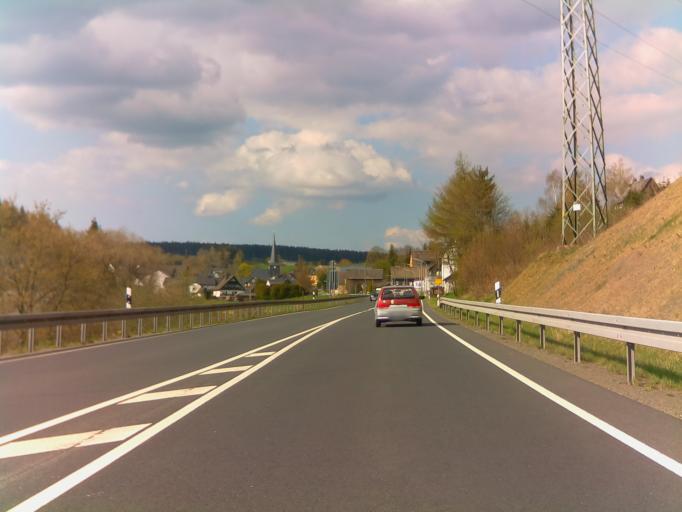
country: DE
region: Bavaria
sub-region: Upper Franconia
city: Teuschnitz
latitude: 50.4256
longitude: 11.3583
